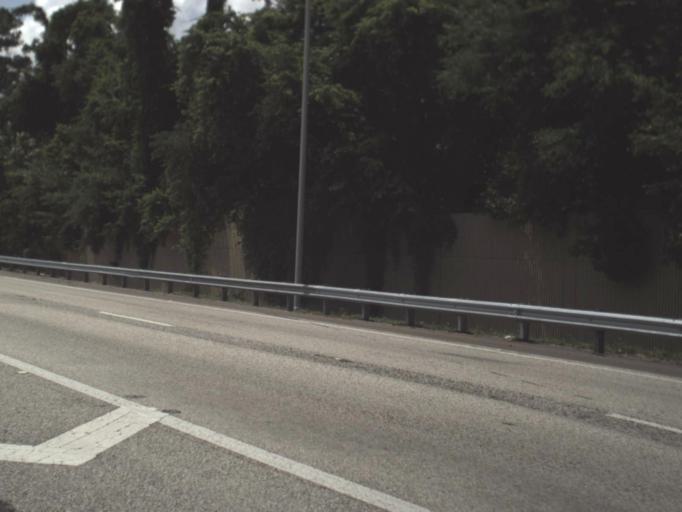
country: US
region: Florida
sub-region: Clay County
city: Orange Park
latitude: 30.1918
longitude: -81.6990
